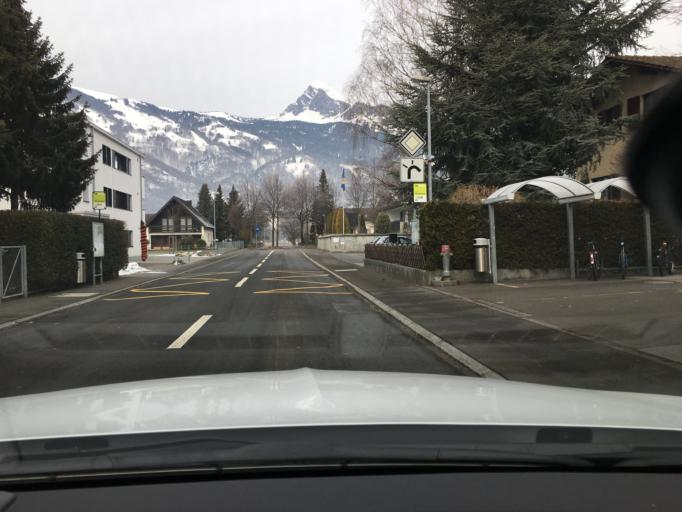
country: LI
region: Balzers
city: Balzers
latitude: 47.0634
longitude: 9.4926
